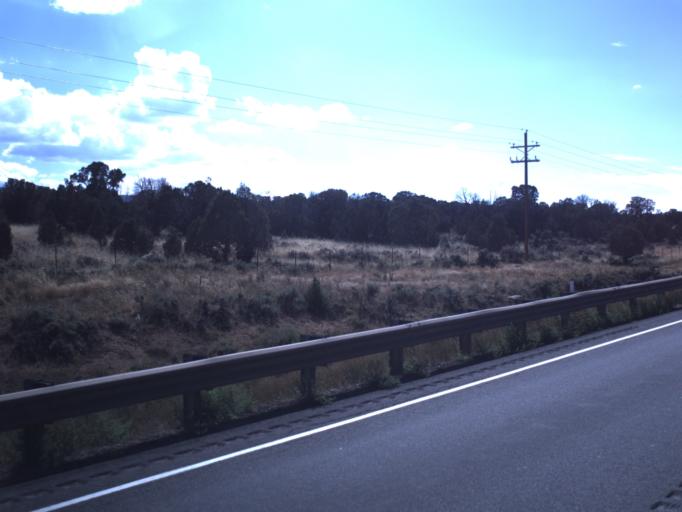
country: US
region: Utah
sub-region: Duchesne County
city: Duchesne
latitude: 40.2081
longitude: -110.8198
